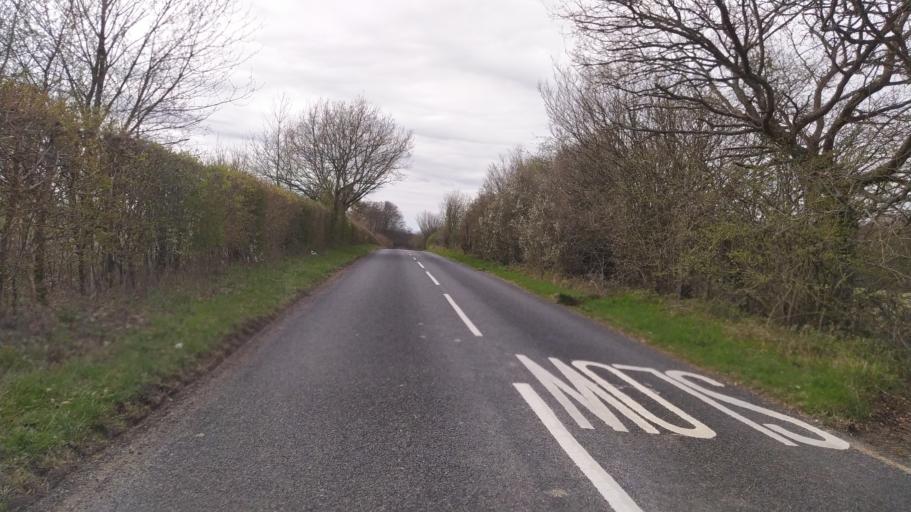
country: GB
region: England
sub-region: Hampshire
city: Bishops Waltham
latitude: 51.0162
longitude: -1.1899
